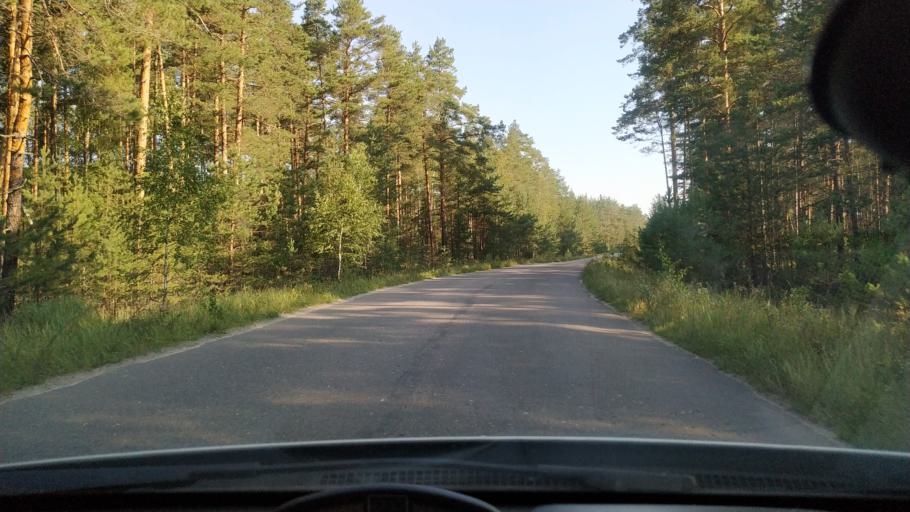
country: RU
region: Moskovskaya
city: Roshal'
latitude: 55.6535
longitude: 39.7994
